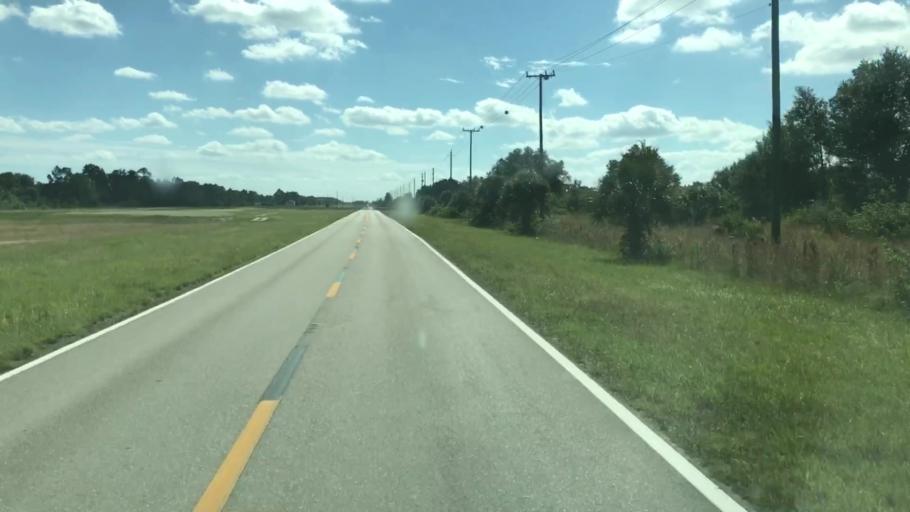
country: US
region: Florida
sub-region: Lee County
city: Lehigh Acres
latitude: 26.6721
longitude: -81.6637
